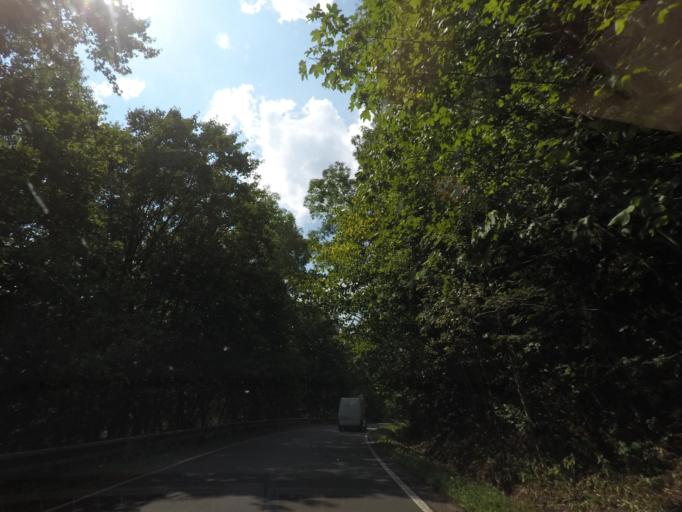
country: CZ
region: Kralovehradecky
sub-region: Okres Trutnov
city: Trutnov
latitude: 50.5884
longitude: 15.9794
